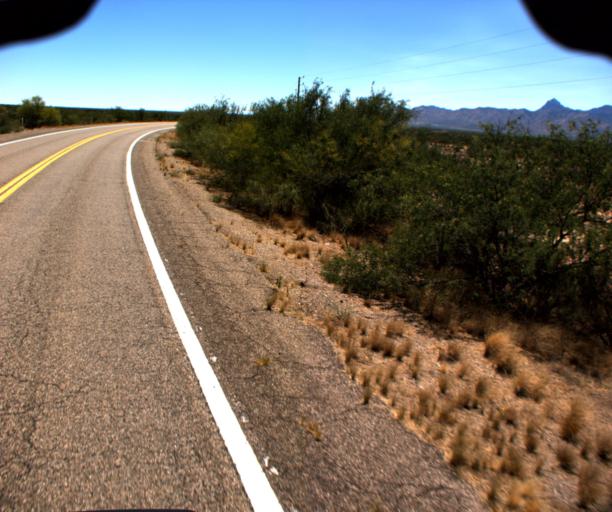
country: US
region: Arizona
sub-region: Pima County
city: Three Points
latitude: 31.8427
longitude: -111.3994
